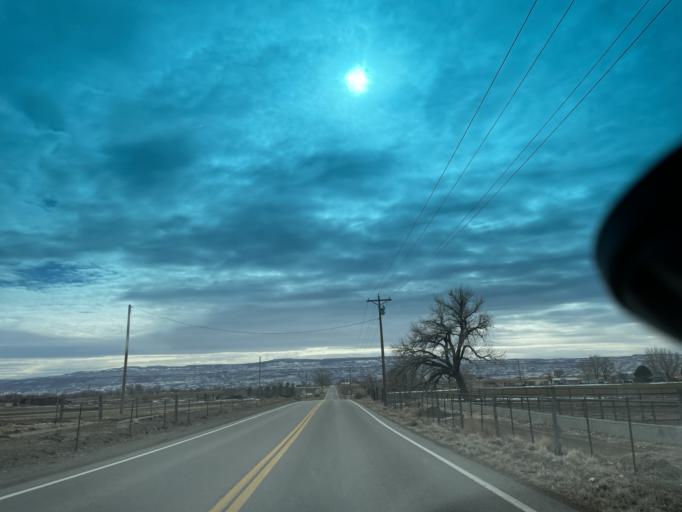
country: US
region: Colorado
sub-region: Mesa County
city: Loma
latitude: 39.2217
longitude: -108.8130
